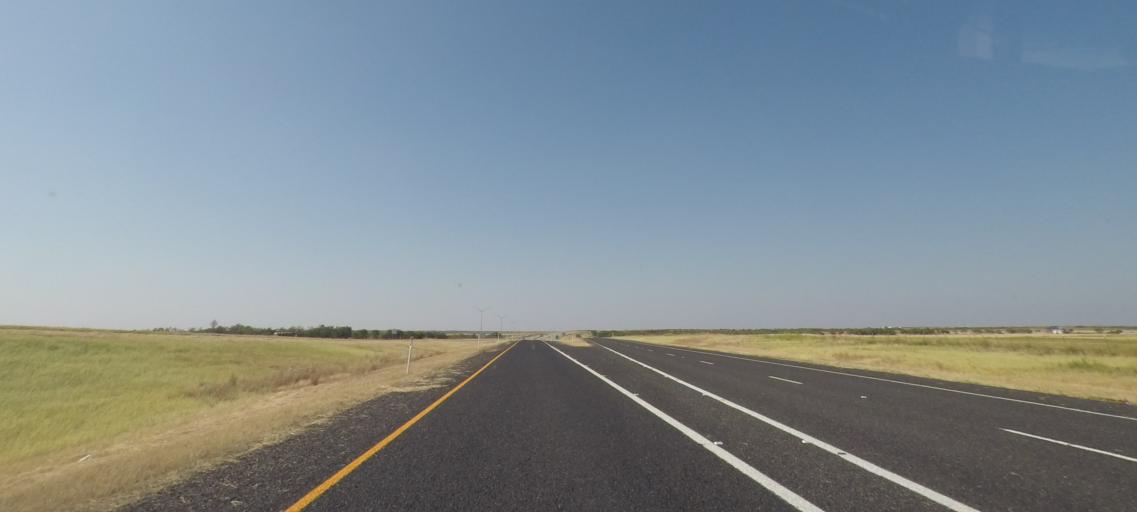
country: US
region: Texas
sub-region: Baylor County
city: Seymour
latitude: 33.5987
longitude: -99.2411
